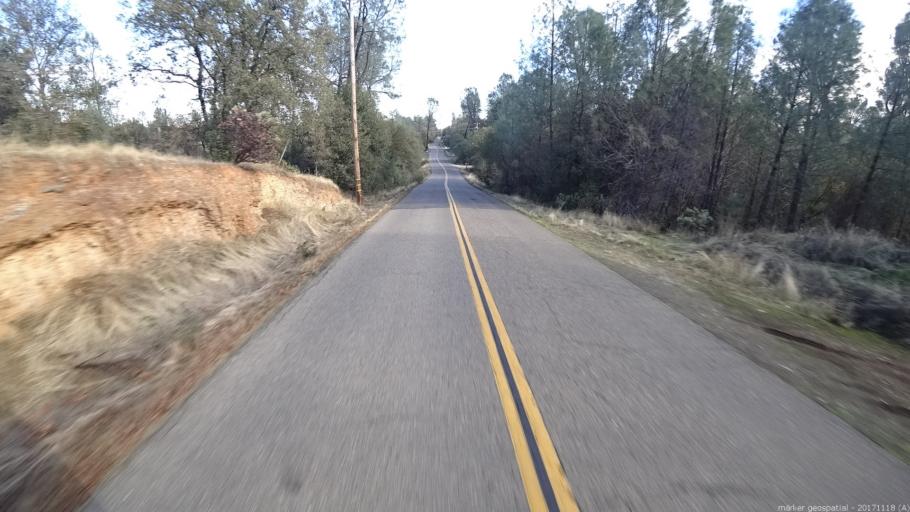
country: US
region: California
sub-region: Shasta County
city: Anderson
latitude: 40.4726
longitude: -122.4099
